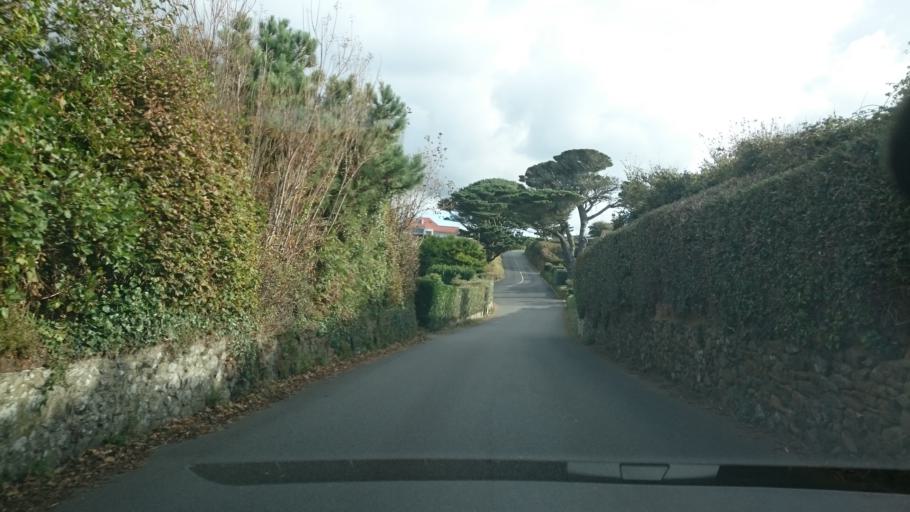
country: GG
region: St Peter Port
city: Saint Peter Port
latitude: 49.4289
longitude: -2.6599
